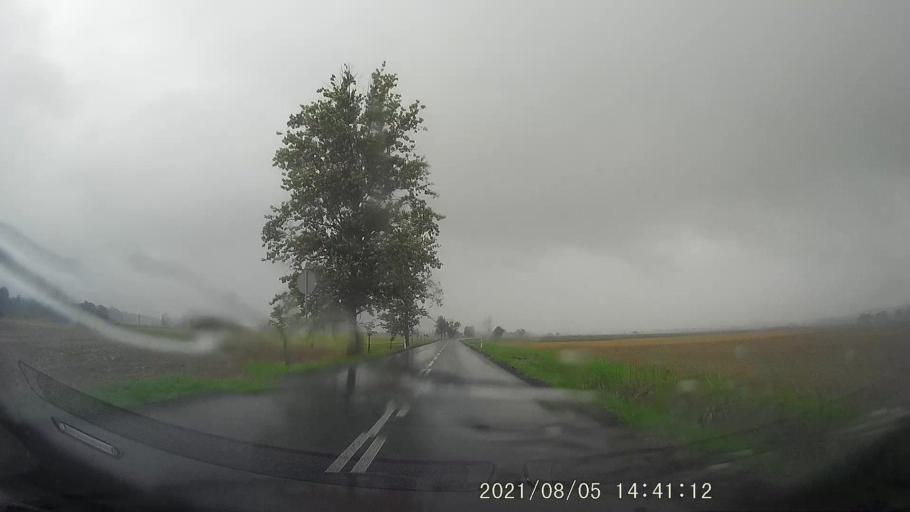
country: PL
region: Opole Voivodeship
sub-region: Powiat nyski
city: Nysa
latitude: 50.4704
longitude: 17.4177
